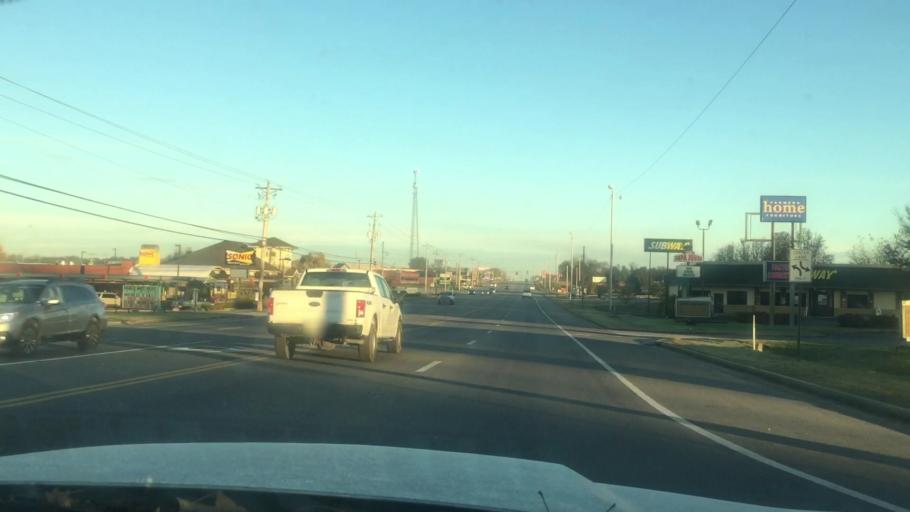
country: US
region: Tennessee
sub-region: Franklin County
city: Decherd
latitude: 35.2097
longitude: -86.0952
